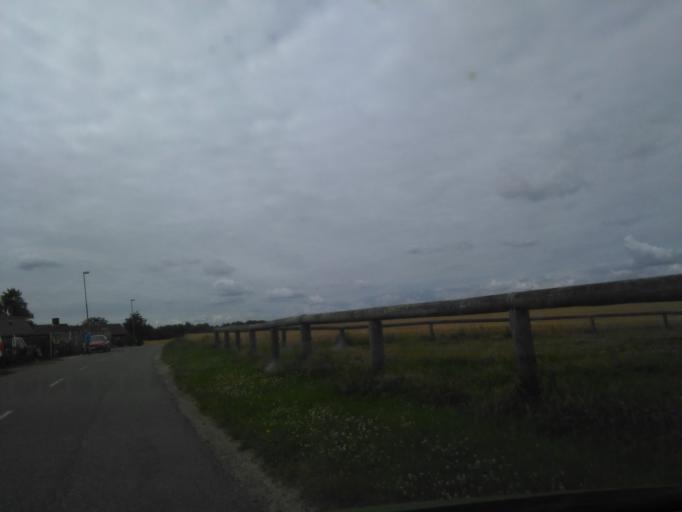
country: DK
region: Central Jutland
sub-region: Arhus Kommune
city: Solbjerg
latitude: 56.0194
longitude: 10.0735
